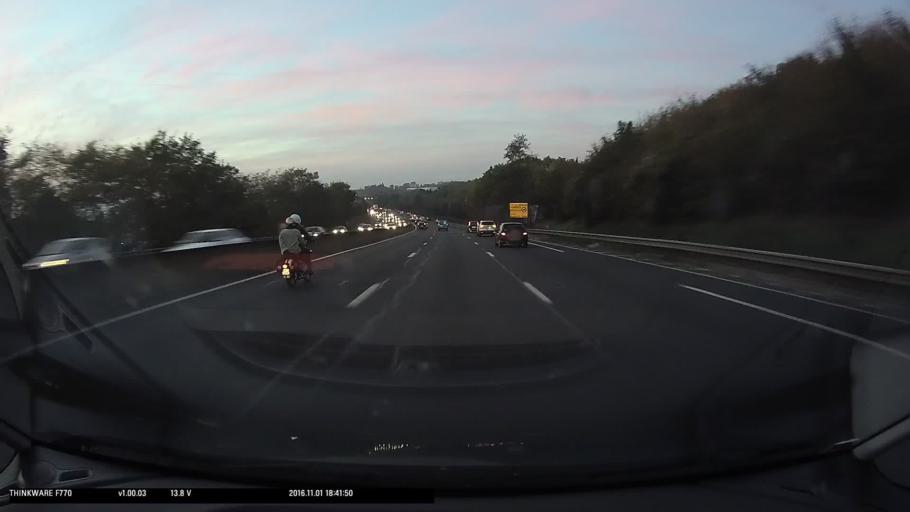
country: FR
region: Ile-de-France
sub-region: Departement de l'Essonne
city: Longjumeau
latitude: 48.6927
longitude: 2.3212
